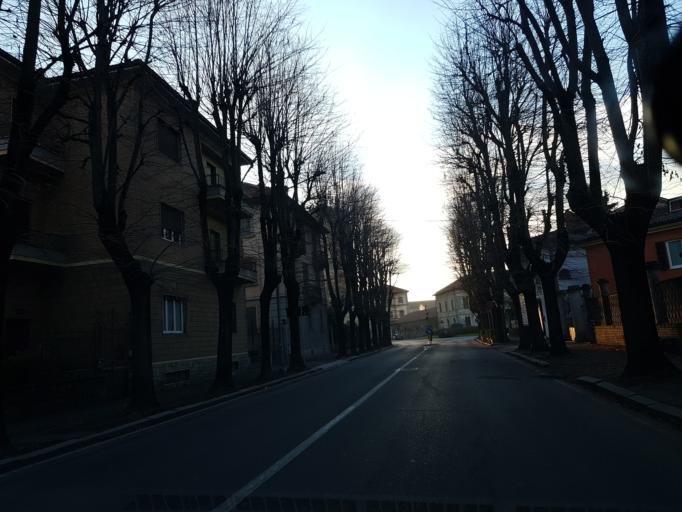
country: IT
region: Piedmont
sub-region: Provincia di Alessandria
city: Novi Ligure
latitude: 44.7631
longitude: 8.7961
